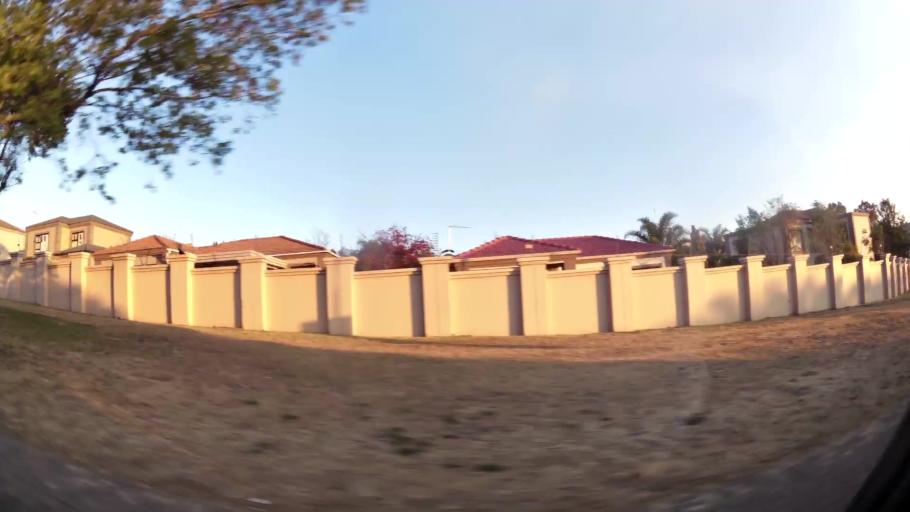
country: ZA
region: Gauteng
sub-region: City of Johannesburg Metropolitan Municipality
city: Diepsloot
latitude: -26.0413
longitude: 27.9879
